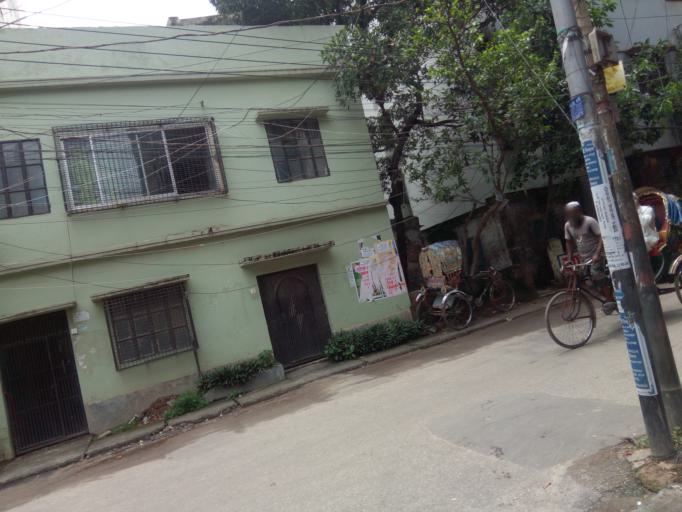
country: BD
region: Dhaka
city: Azimpur
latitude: 23.7573
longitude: 90.3656
